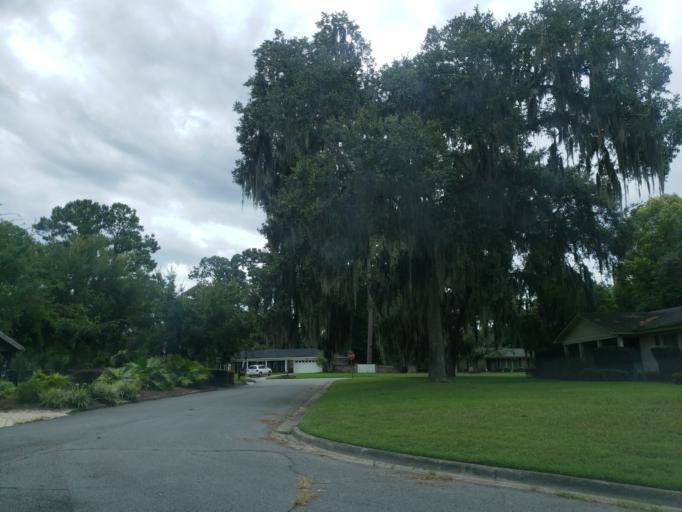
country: US
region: Georgia
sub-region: Chatham County
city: Isle of Hope
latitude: 31.9927
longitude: -81.0547
